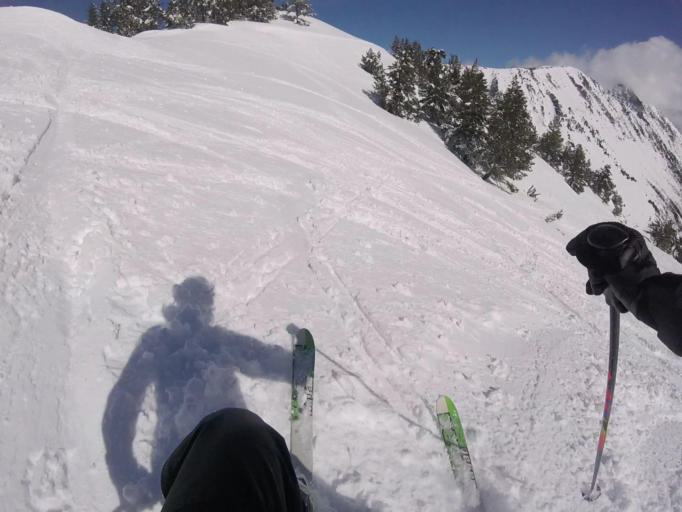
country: ES
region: Catalonia
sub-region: Provincia de Lleida
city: Espot
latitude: 42.6486
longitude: 0.9922
